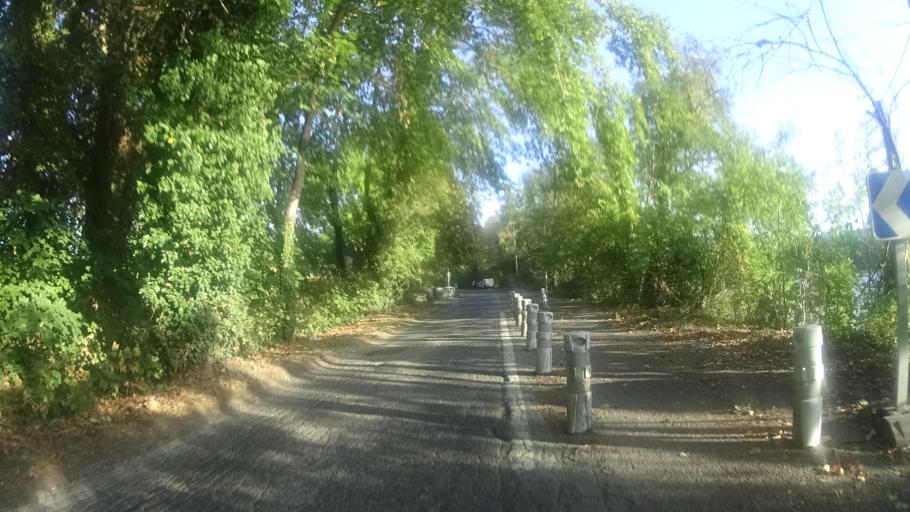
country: FR
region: Ile-de-France
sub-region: Departement de l'Essonne
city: Evry
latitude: 48.6323
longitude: 2.4587
